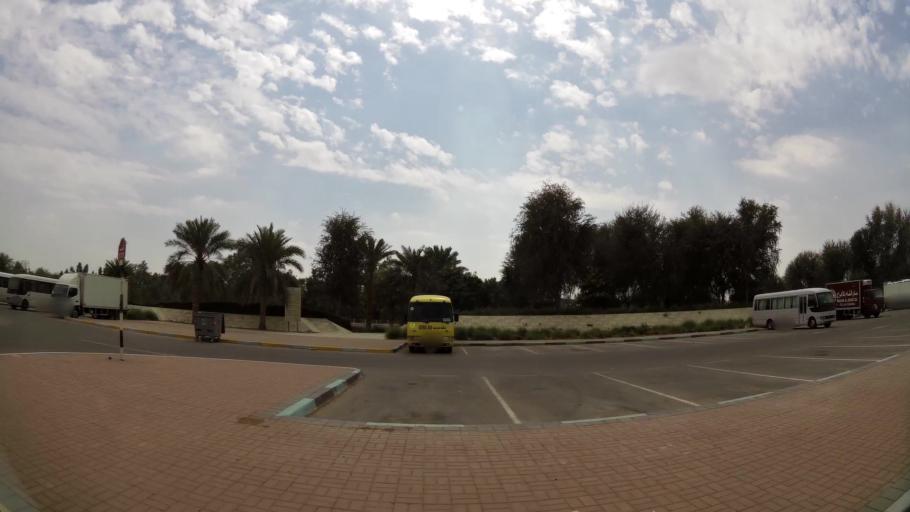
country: AE
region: Abu Dhabi
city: Al Ain
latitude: 24.2104
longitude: 55.7821
